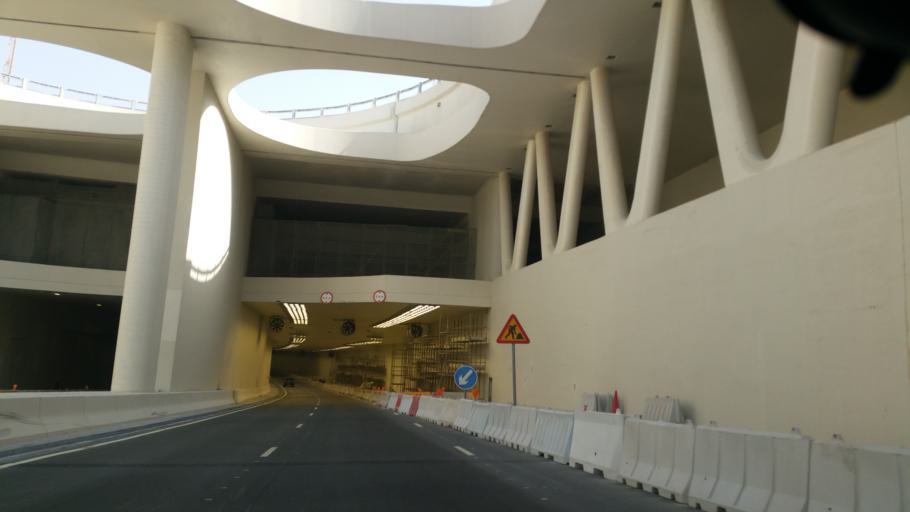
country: QA
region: Baladiyat Umm Salal
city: Umm Salal Muhammad
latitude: 25.4202
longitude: 51.5059
